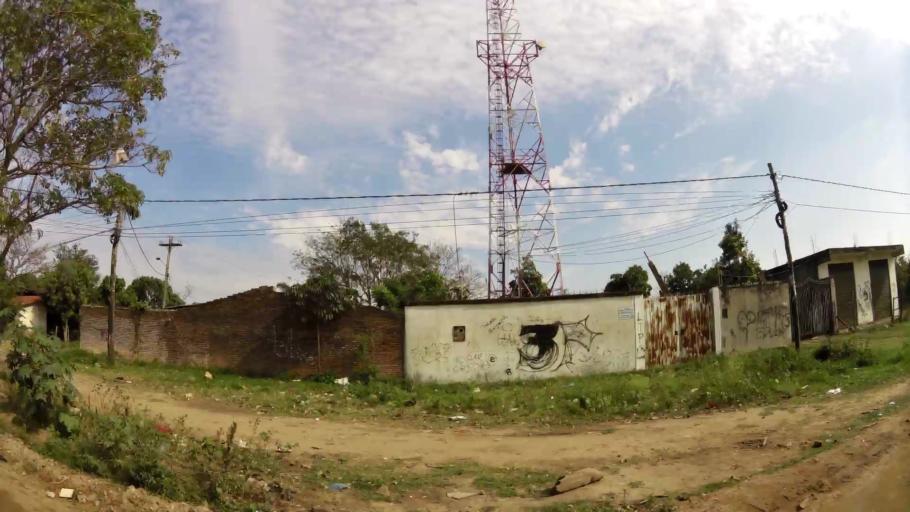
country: BO
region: Santa Cruz
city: Santa Cruz de la Sierra
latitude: -17.7253
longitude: -63.1375
